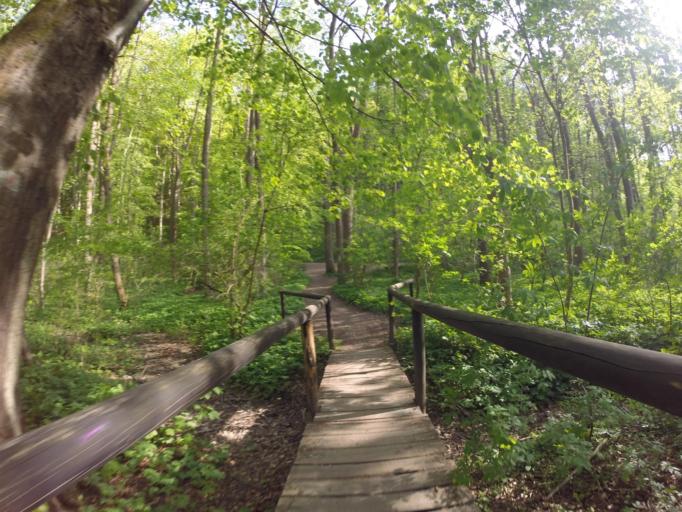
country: DE
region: Thuringia
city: Zollnitz
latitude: 50.9067
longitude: 11.6337
